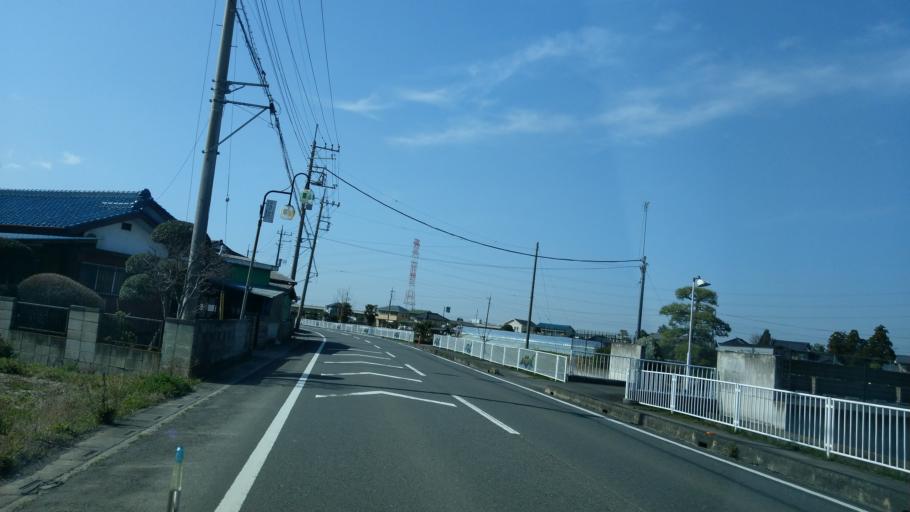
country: JP
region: Saitama
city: Kawagoe
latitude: 35.9828
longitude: 139.4810
